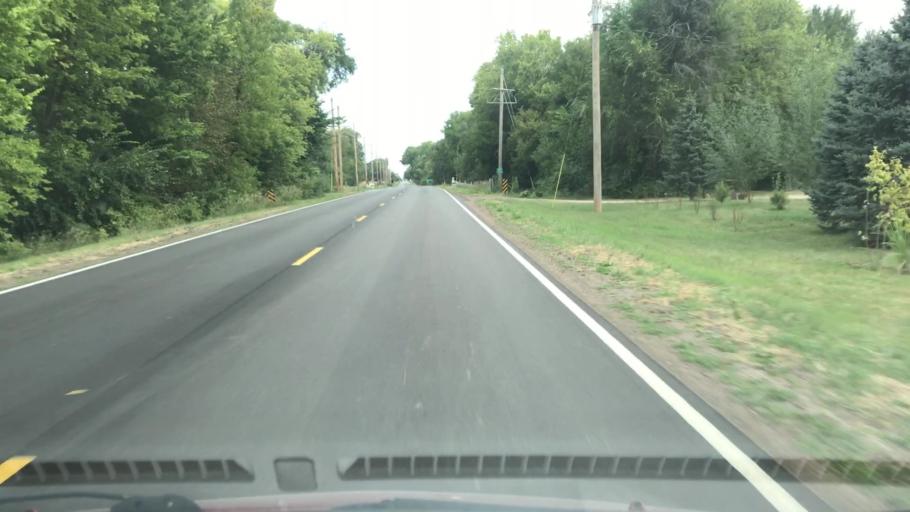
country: US
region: Nebraska
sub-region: Hall County
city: Grand Island
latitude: 40.9225
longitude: -98.3016
